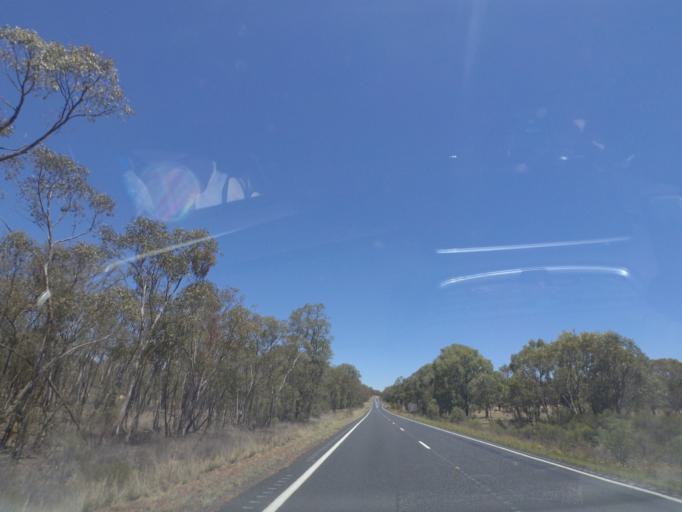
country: AU
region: New South Wales
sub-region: Warrumbungle Shire
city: Coonabarabran
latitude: -31.2229
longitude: 149.3239
